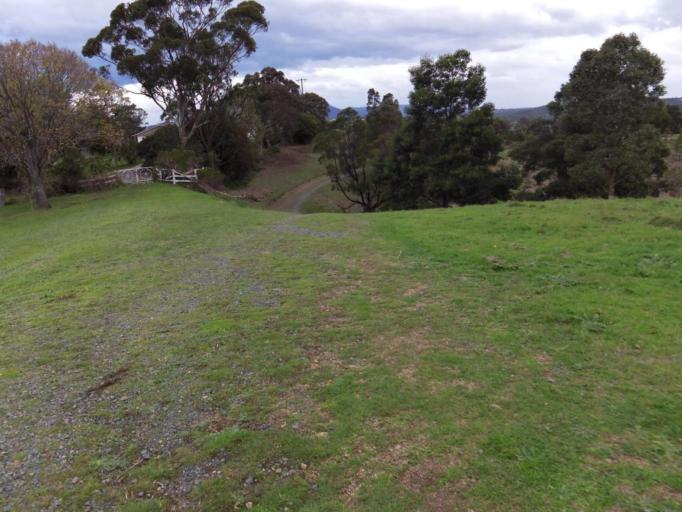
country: AU
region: Victoria
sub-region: Yarra Ranges
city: Chirnside Park
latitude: -37.7161
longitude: 145.2899
